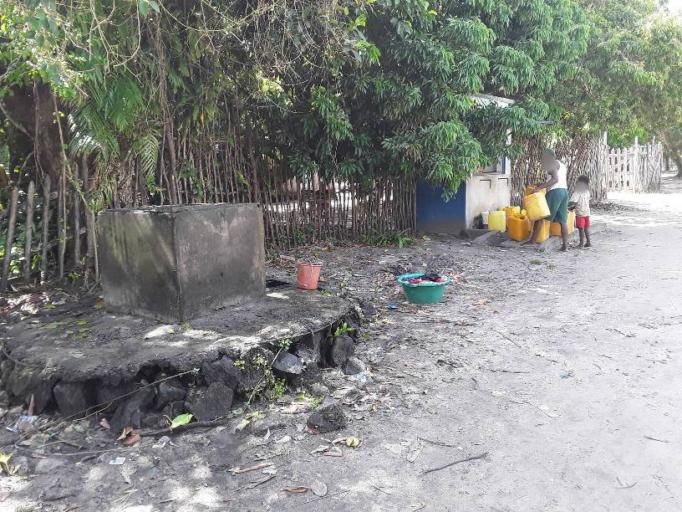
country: MG
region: Atsinanana
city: Andovoranto
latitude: -19.3286
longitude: 48.9775
